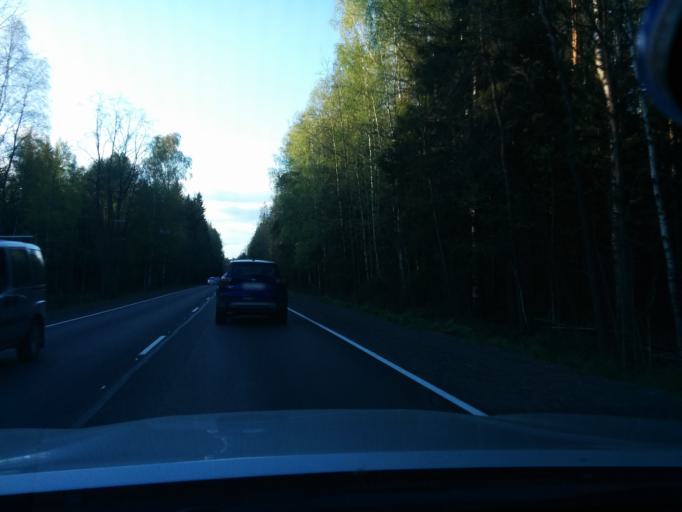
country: RU
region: Leningrad
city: Verkhniye Osel'ki
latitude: 60.2066
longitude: 30.4264
